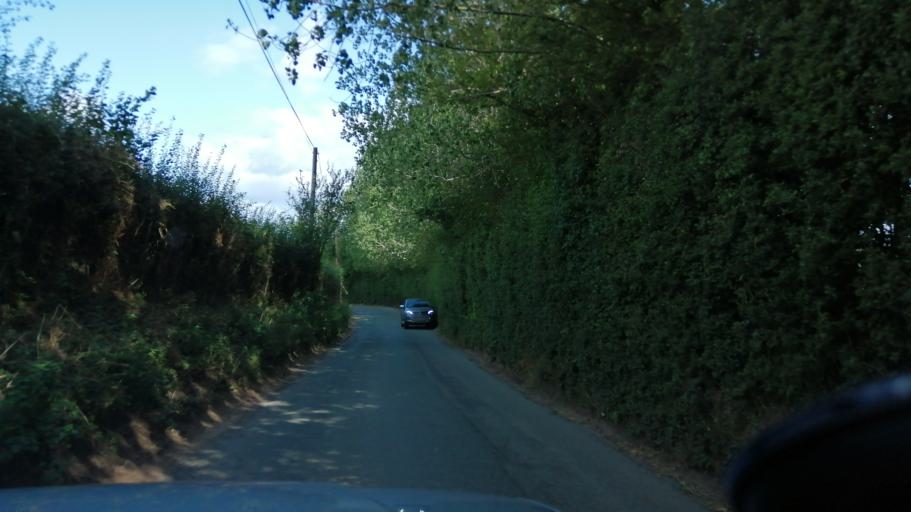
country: GB
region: England
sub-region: Herefordshire
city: Bridge Sollers
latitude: 52.0611
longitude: -2.8613
